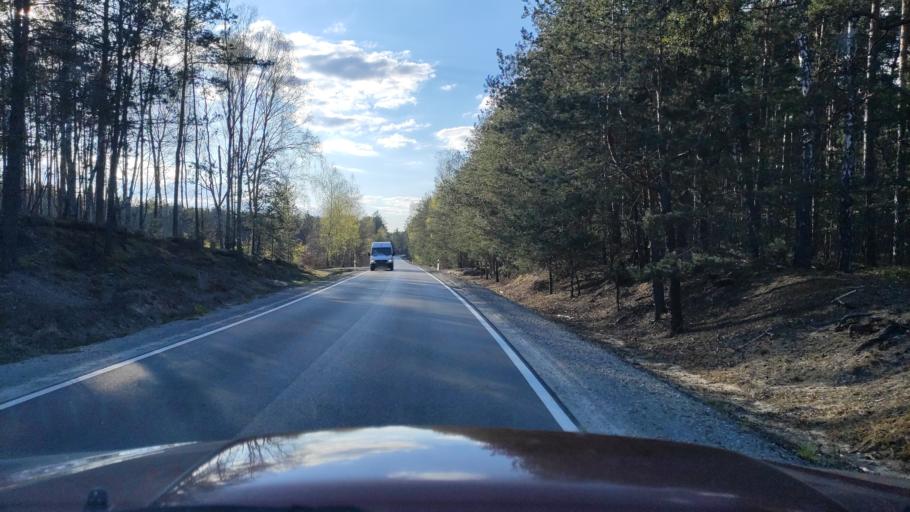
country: PL
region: Masovian Voivodeship
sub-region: Powiat zwolenski
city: Zwolen
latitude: 51.4067
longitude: 21.5264
